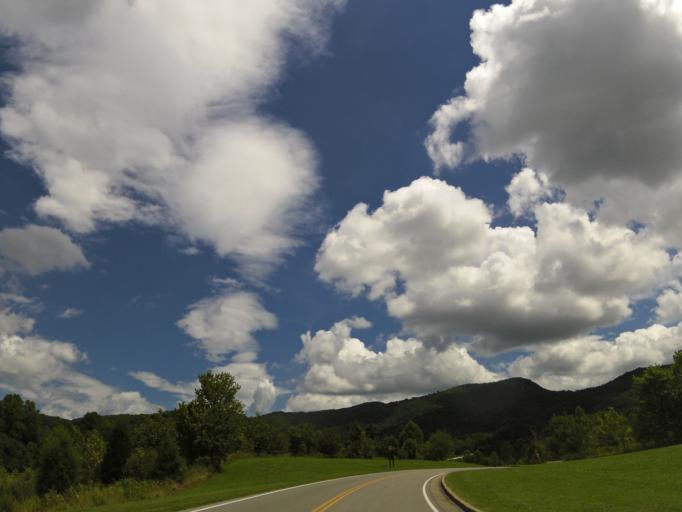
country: US
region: Kentucky
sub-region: Bell County
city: Middlesboro
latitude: 36.6041
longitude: -83.6966
